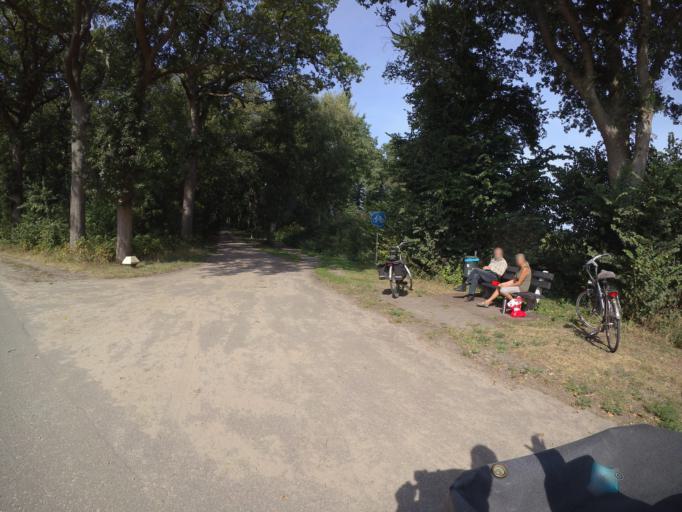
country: NL
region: Drenthe
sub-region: Gemeente Westerveld
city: Havelte
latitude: 52.7661
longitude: 6.2123
